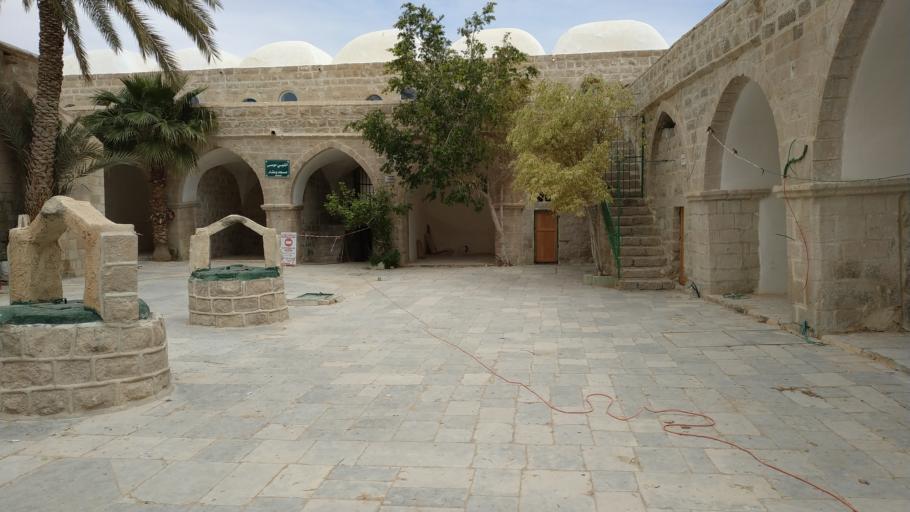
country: PS
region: West Bank
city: Jericho
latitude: 31.7863
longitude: 35.4315
